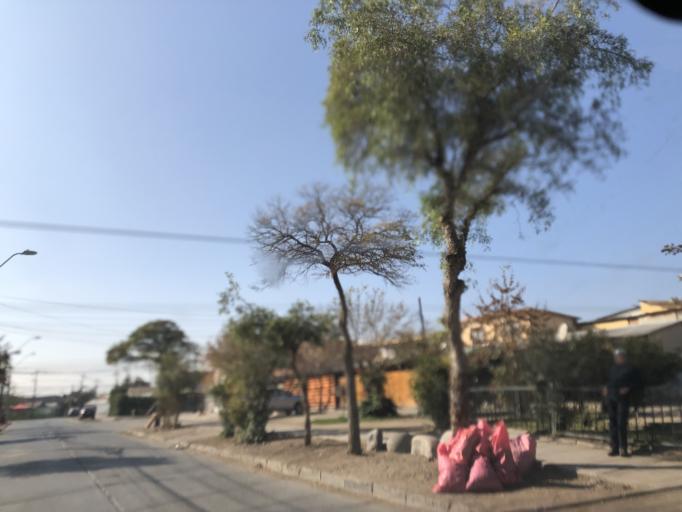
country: CL
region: Santiago Metropolitan
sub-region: Provincia de Cordillera
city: Puente Alto
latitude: -33.6202
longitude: -70.5912
